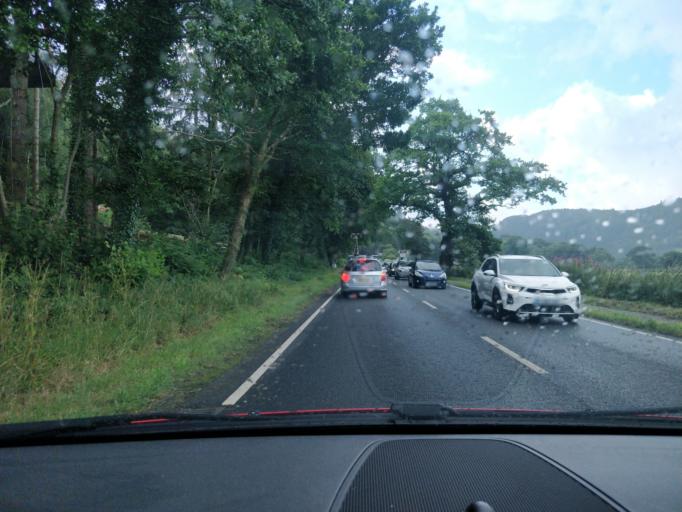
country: GB
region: Wales
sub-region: Conwy
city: Betws-y-Coed
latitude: 53.1017
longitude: -3.7874
